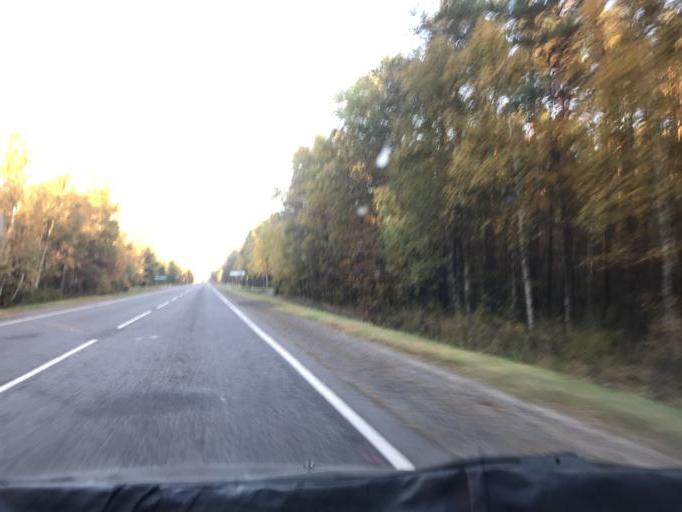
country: BY
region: Gomel
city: Pyetrykaw
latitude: 52.2748
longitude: 28.1932
